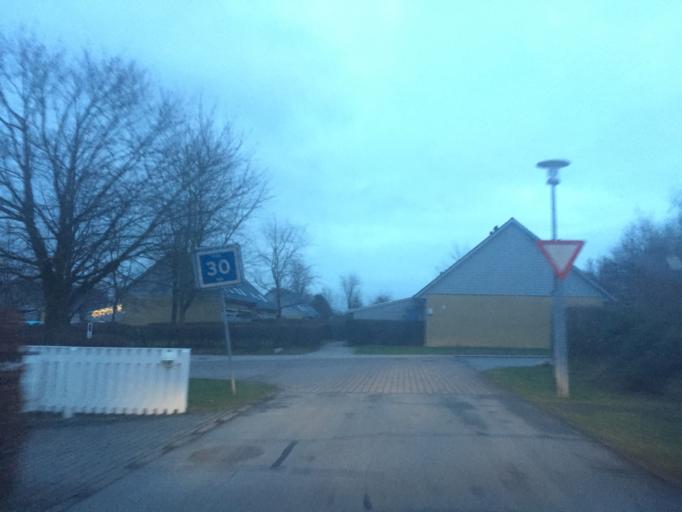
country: DK
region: Capital Region
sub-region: Hoje-Taastrup Kommune
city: Flong
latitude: 55.6420
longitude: 12.1983
